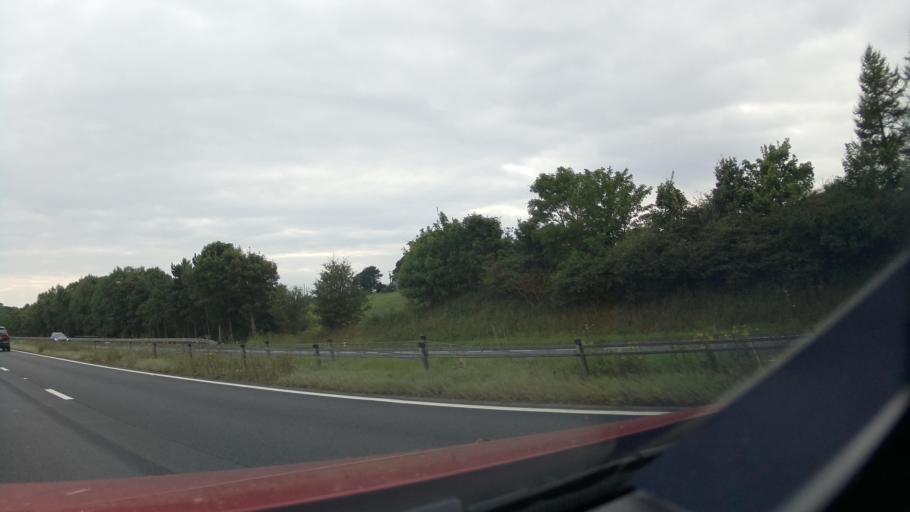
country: GB
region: England
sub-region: County Durham
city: Bishop Middleham
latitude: 54.6563
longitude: -1.5055
